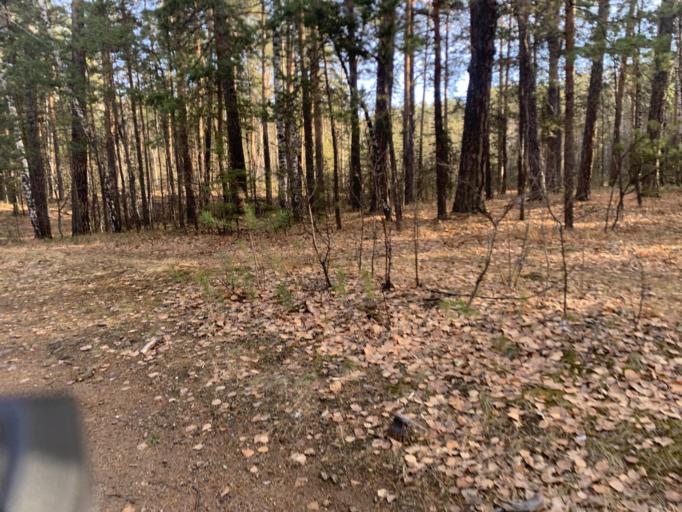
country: RU
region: Chelyabinsk
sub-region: Gorod Chelyabinsk
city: Chelyabinsk
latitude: 55.1540
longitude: 61.3502
